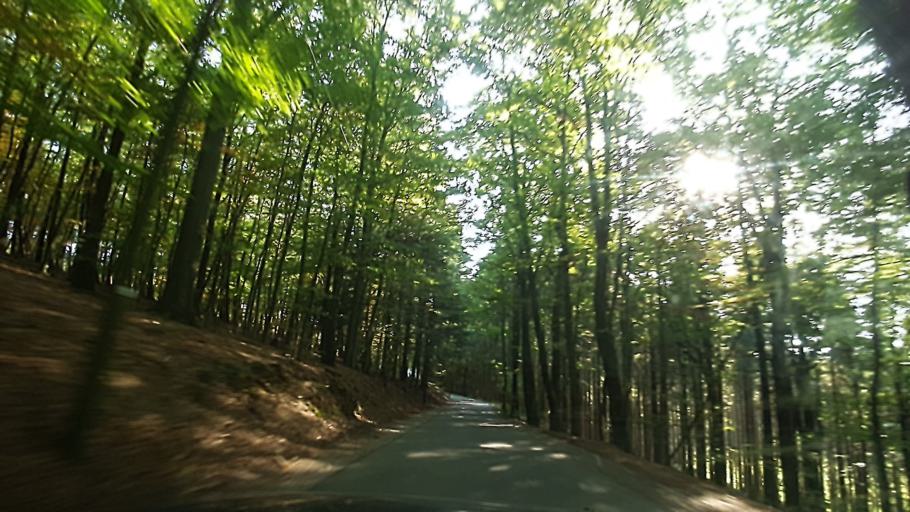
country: DE
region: North Rhine-Westphalia
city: Halver
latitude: 51.1330
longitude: 7.4833
